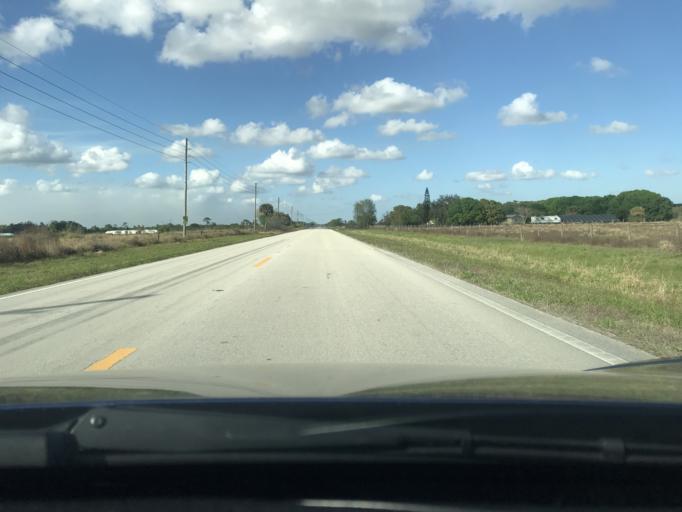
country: US
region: Florida
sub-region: Okeechobee County
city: Taylor Creek
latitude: 27.2488
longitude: -80.6945
